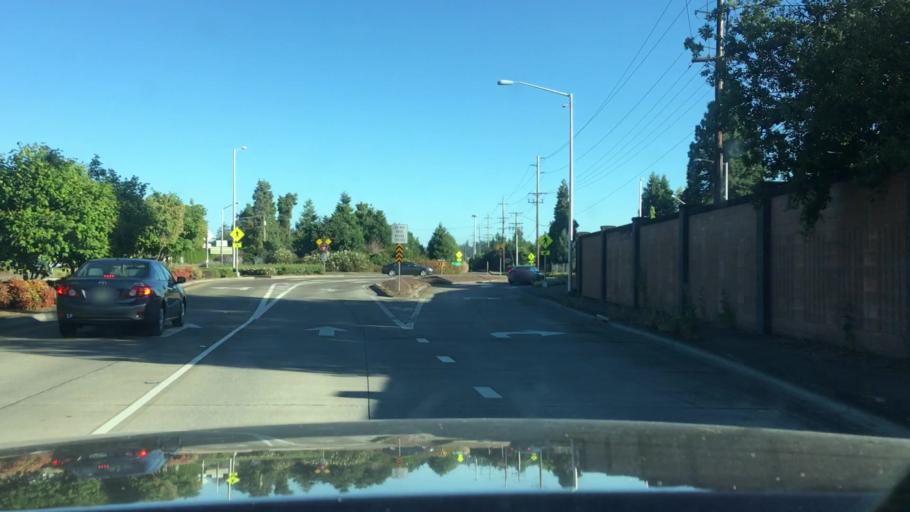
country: US
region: Oregon
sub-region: Lane County
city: Springfield
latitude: 44.0718
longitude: -123.0294
